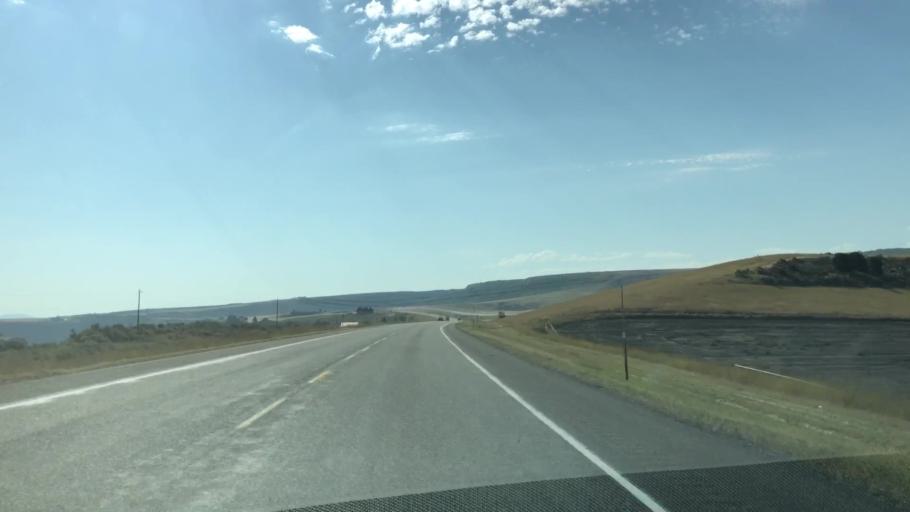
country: US
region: Idaho
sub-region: Madison County
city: Rexburg
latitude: 43.6013
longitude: -111.6512
